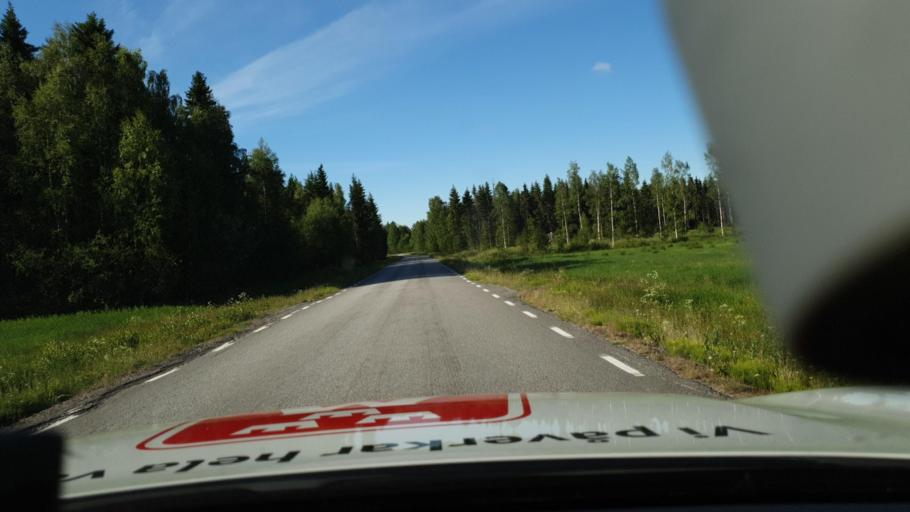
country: SE
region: Norrbotten
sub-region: Kalix Kommun
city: Toere
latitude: 65.8651
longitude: 22.6765
